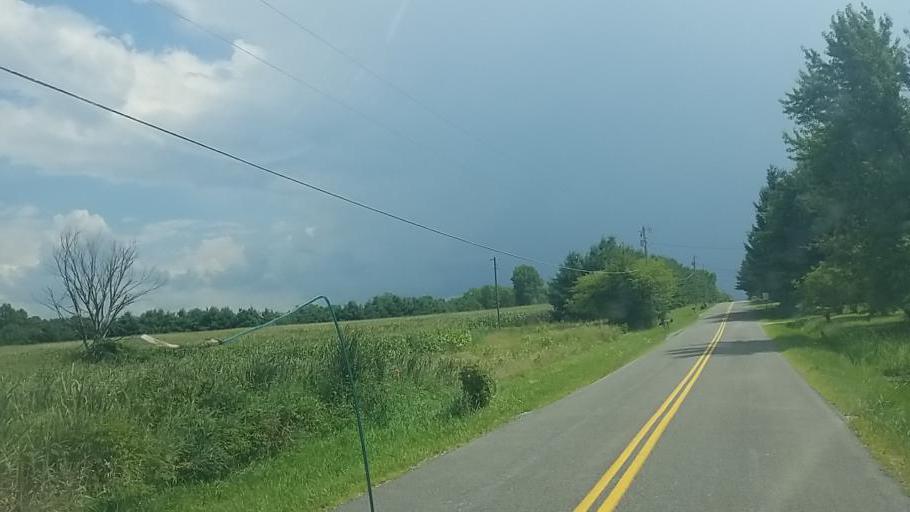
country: US
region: Ohio
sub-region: Medina County
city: Westfield Center
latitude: 41.0965
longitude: -81.9623
